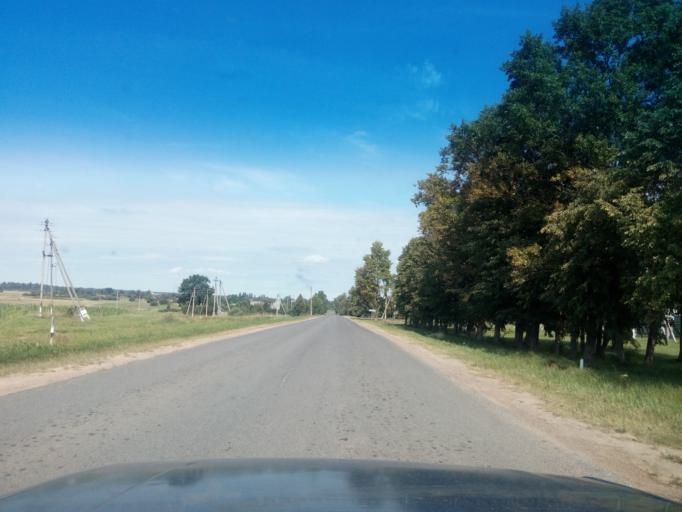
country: BY
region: Vitebsk
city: Vyerkhnyadzvinsk
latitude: 55.8226
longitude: 27.7347
